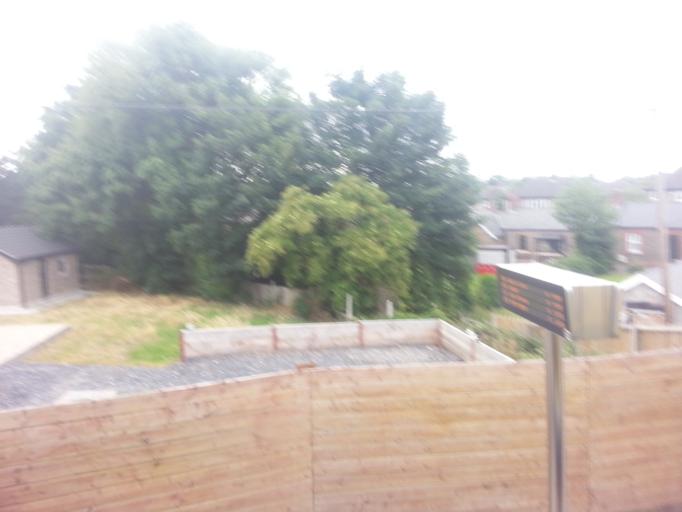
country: IE
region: Leinster
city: Cabra
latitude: 53.3651
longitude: -6.3091
